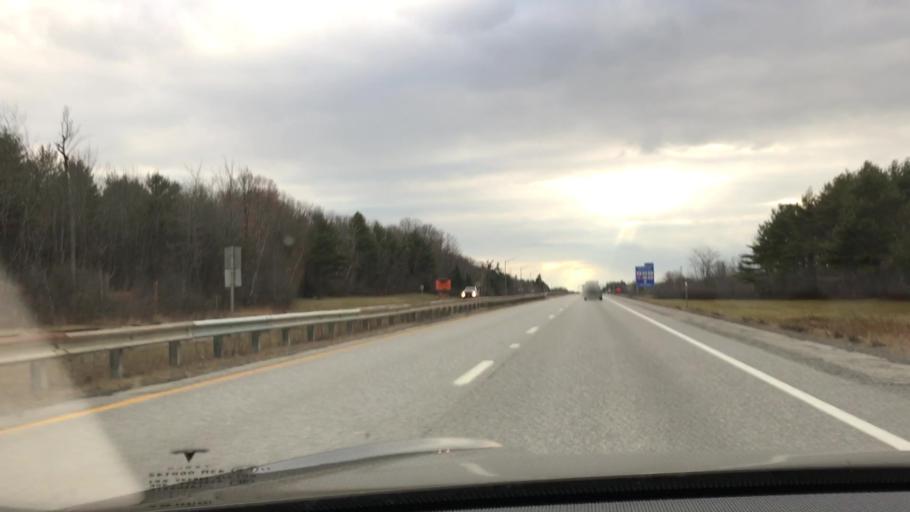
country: US
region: Maine
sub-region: Kennebec County
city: Gardiner
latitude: 44.2299
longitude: -69.8127
